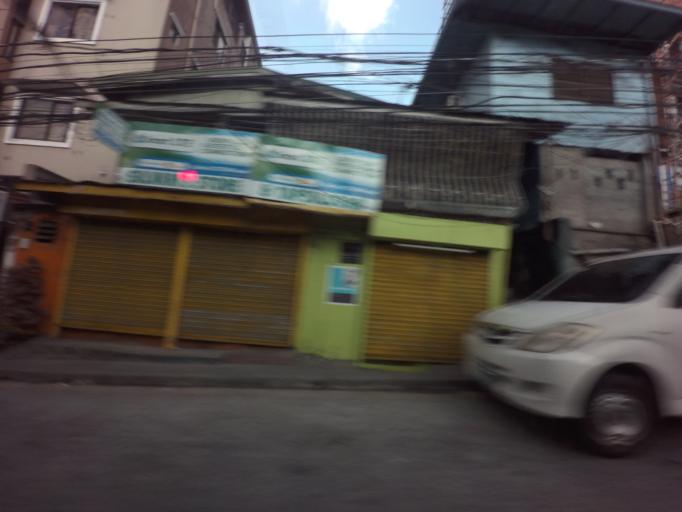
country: PH
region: Metro Manila
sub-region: Mandaluyong
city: Mandaluyong City
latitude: 14.5646
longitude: 121.0479
